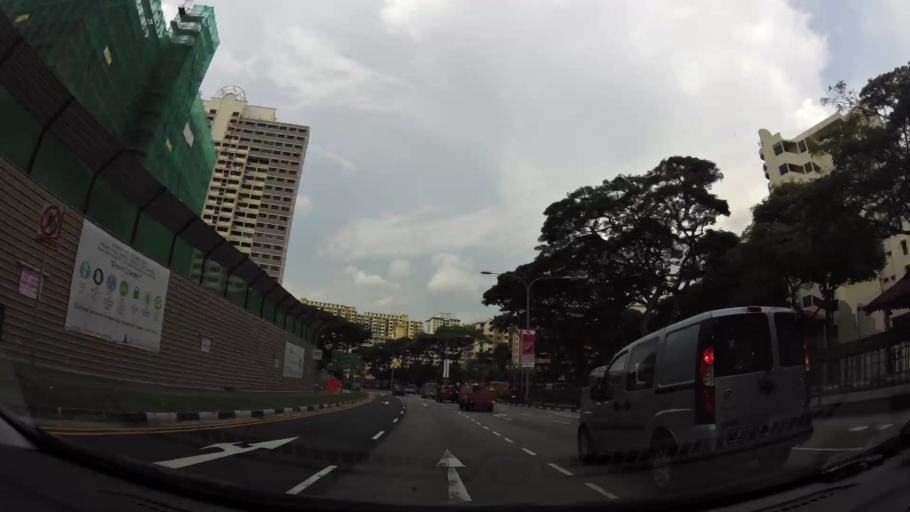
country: SG
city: Singapore
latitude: 1.3335
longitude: 103.8562
